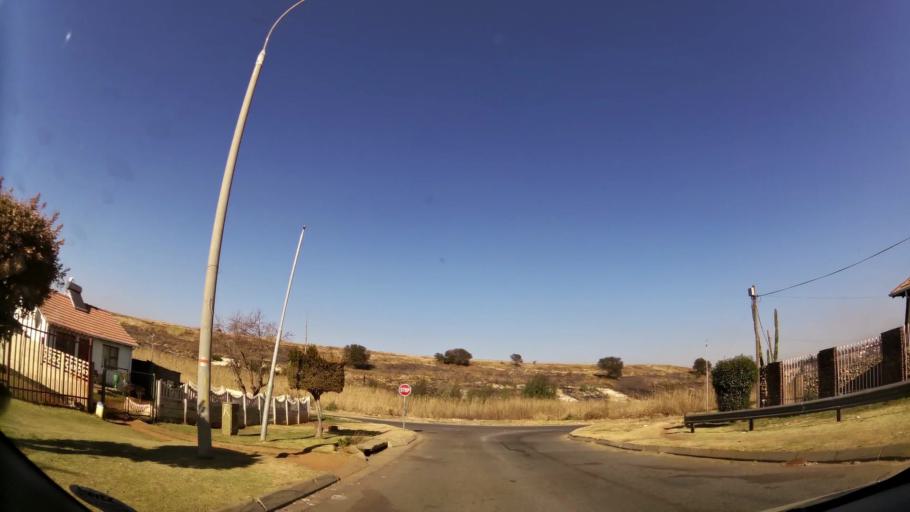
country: ZA
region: Gauteng
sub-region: City of Johannesburg Metropolitan Municipality
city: Roodepoort
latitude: -26.1582
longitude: 27.8456
